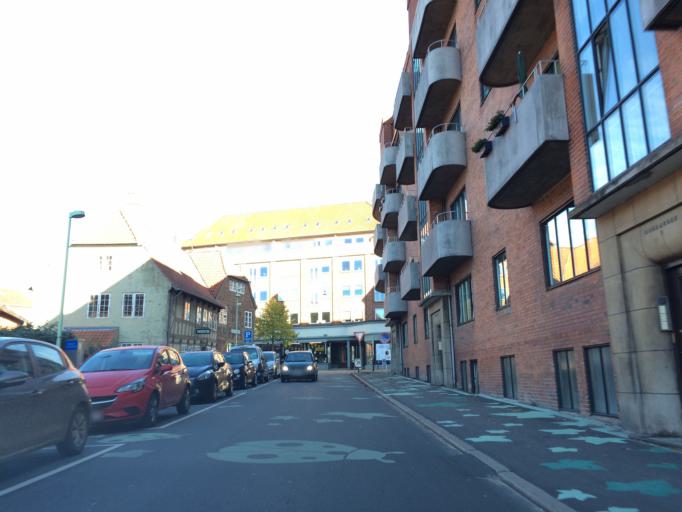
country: DK
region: Central Jutland
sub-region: Randers Kommune
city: Randers
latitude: 56.4595
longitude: 10.0334
